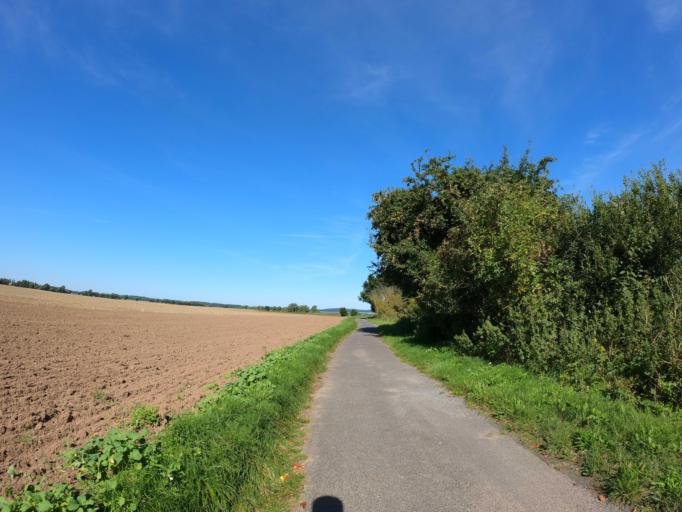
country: DE
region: Mecklenburg-Vorpommern
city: Prohn
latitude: 54.3837
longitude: 13.0419
